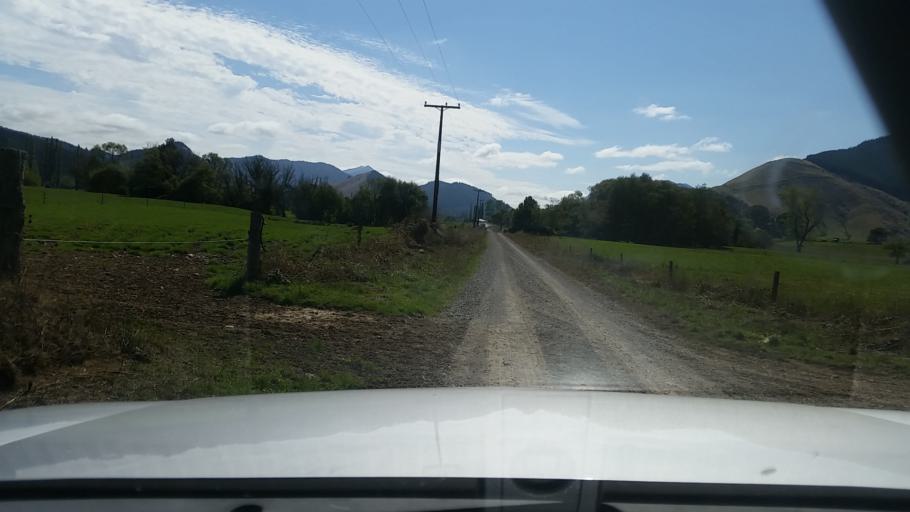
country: NZ
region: Nelson
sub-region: Nelson City
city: Nelson
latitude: -41.2553
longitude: 173.5823
